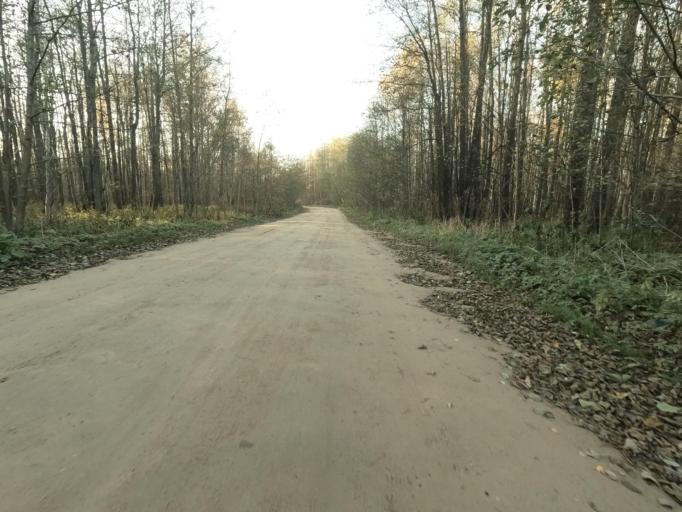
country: RU
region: Leningrad
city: Kirovsk
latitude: 59.8783
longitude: 31.0387
